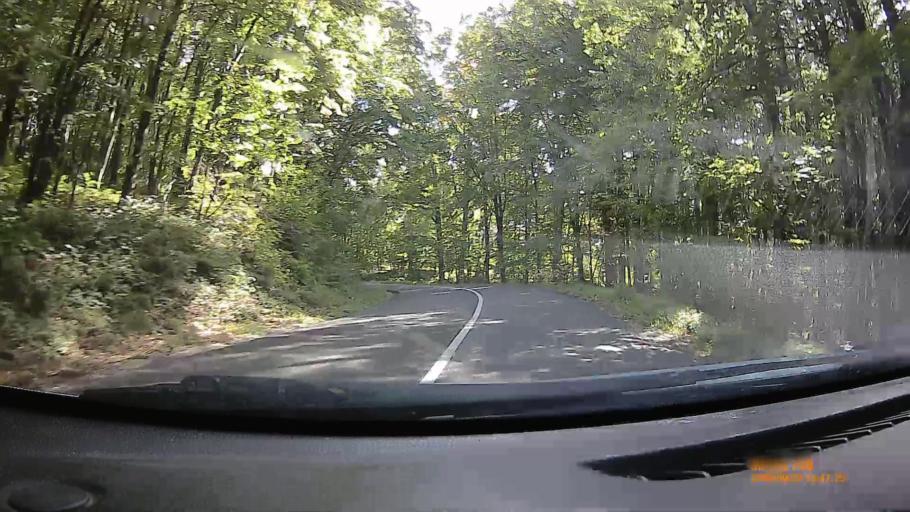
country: HU
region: Borsod-Abauj-Zemplen
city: Saly
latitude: 48.0645
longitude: 20.5756
